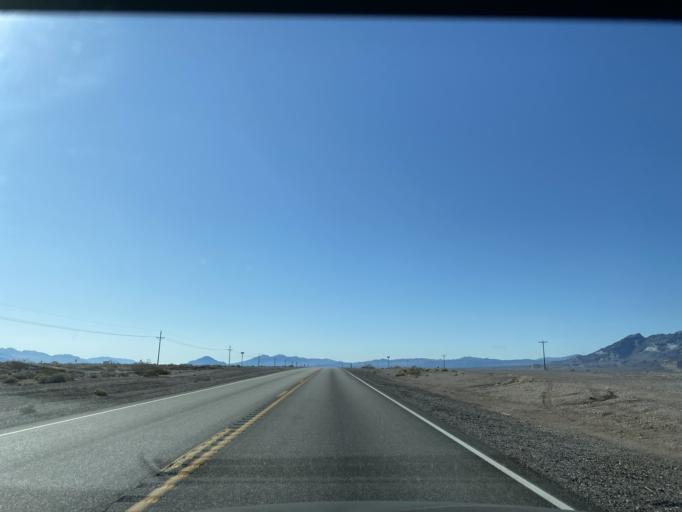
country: US
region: Nevada
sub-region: Nye County
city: Pahrump
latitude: 36.4496
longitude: -116.4219
